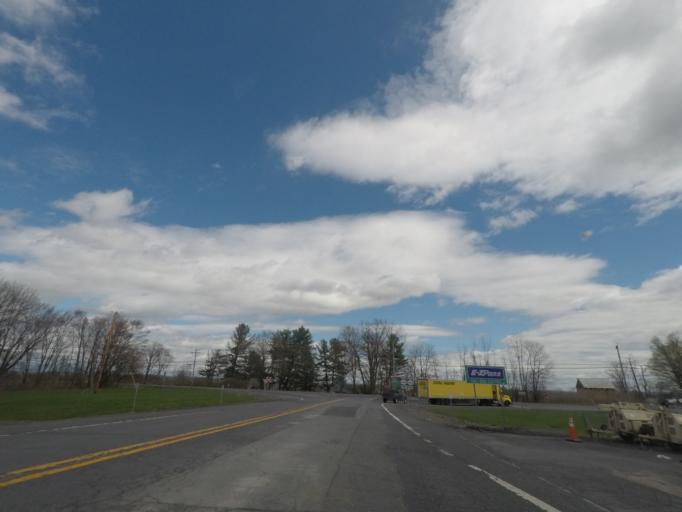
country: US
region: New York
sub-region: Rensselaer County
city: Castleton-on-Hudson
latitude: 42.5340
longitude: -73.7794
